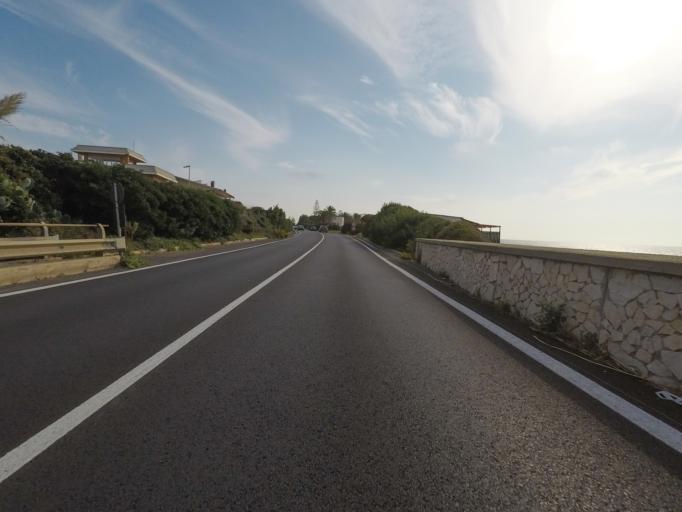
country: IT
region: Latium
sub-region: Citta metropolitana di Roma Capitale
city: Civitavecchia
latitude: 42.0512
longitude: 11.8204
